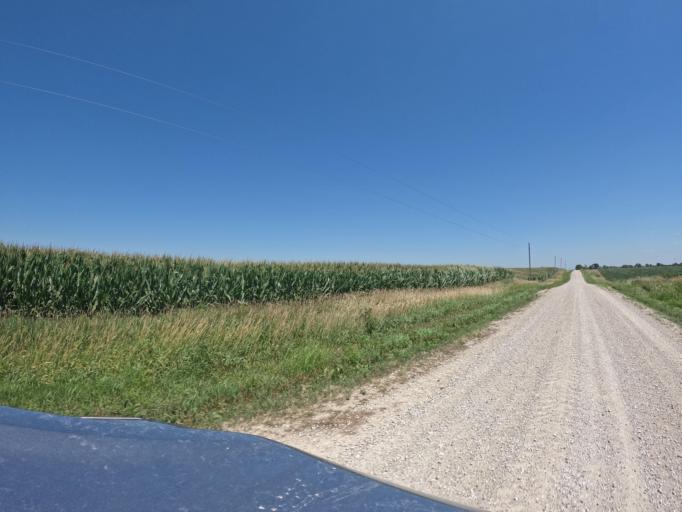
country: US
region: Iowa
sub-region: Keokuk County
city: Sigourney
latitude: 41.4235
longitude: -92.3201
